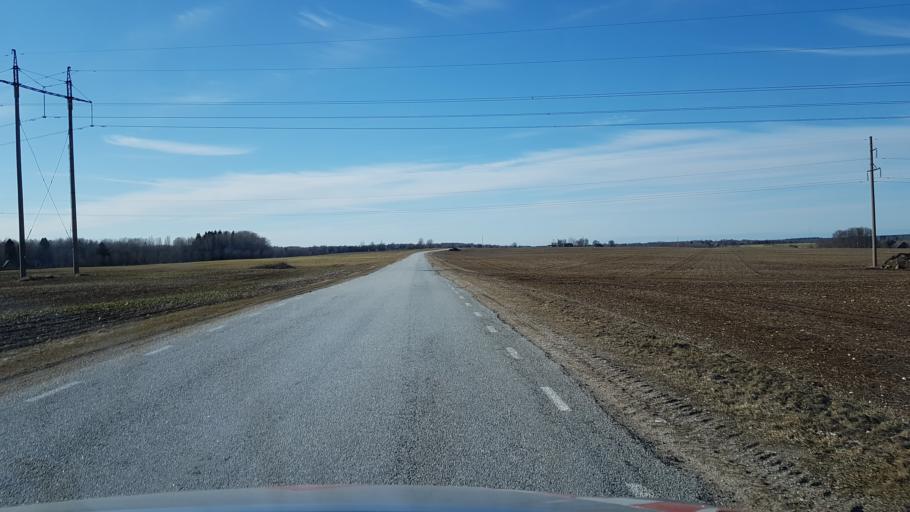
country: EE
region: Laeaene-Virumaa
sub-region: Kadrina vald
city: Kadrina
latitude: 59.2827
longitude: 26.1846
